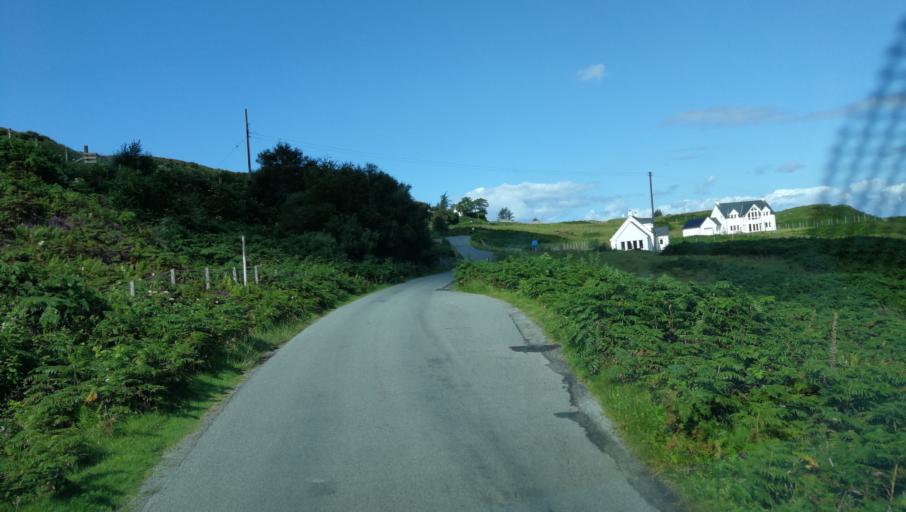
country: GB
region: Scotland
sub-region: Highland
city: Isle of Skye
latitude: 57.4491
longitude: -6.6523
